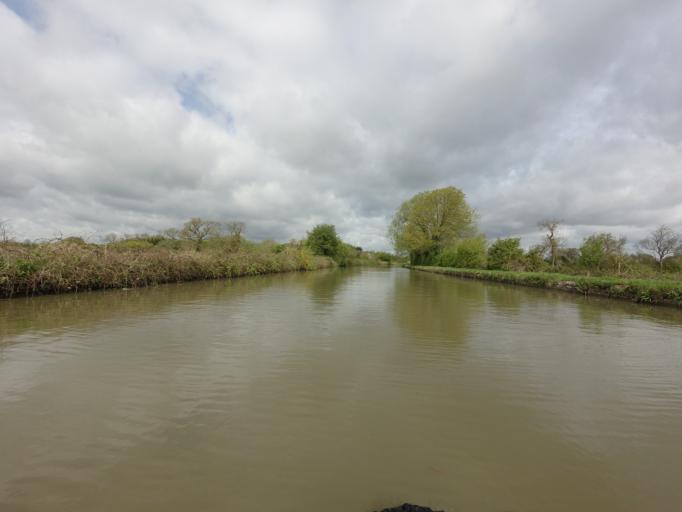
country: GB
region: England
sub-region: Milton Keynes
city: Water Eaton
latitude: 51.9594
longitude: -0.7087
